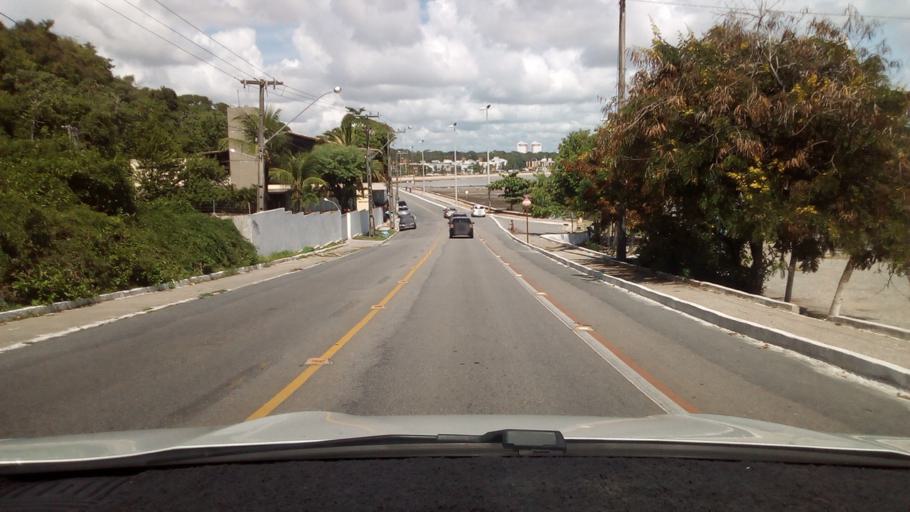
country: BR
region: Paraiba
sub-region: Joao Pessoa
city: Joao Pessoa
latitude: -7.1459
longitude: -34.8032
